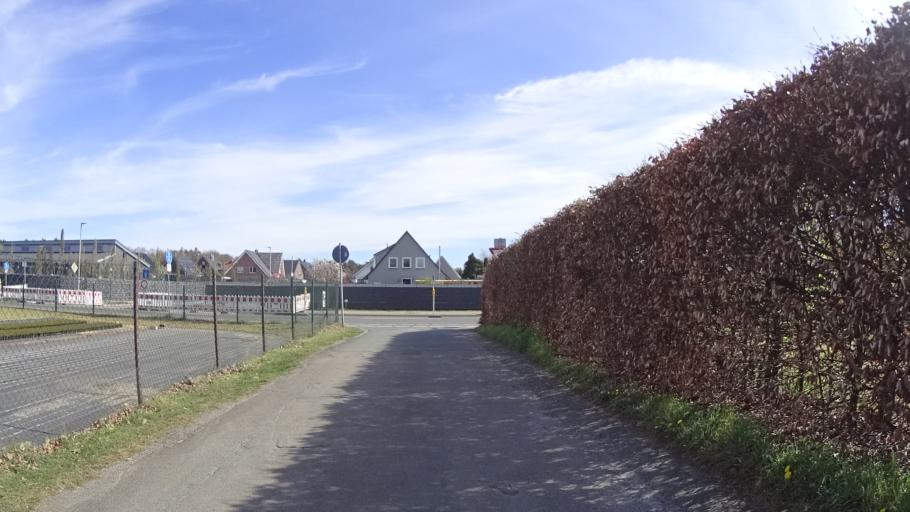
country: DE
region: North Rhine-Westphalia
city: Emsdetten
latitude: 52.2343
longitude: 7.5111
